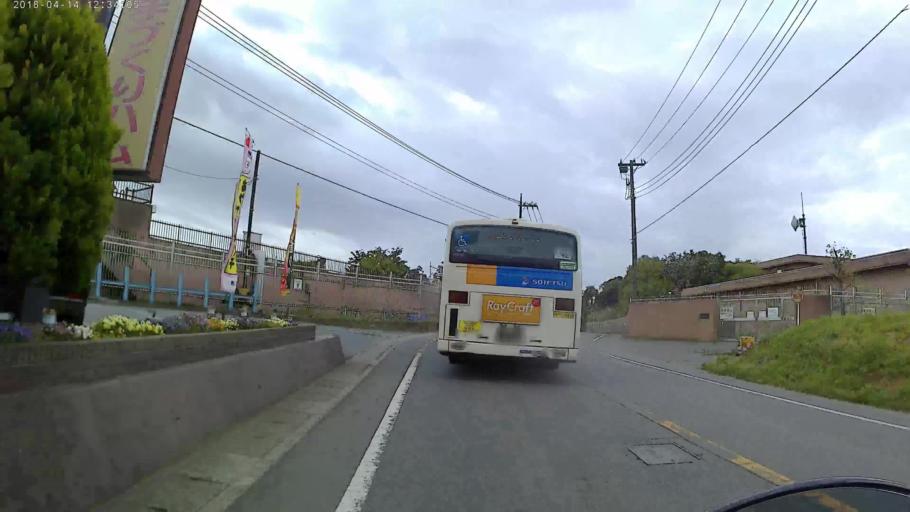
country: JP
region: Kanagawa
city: Atsugi
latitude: 35.4288
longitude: 139.4099
